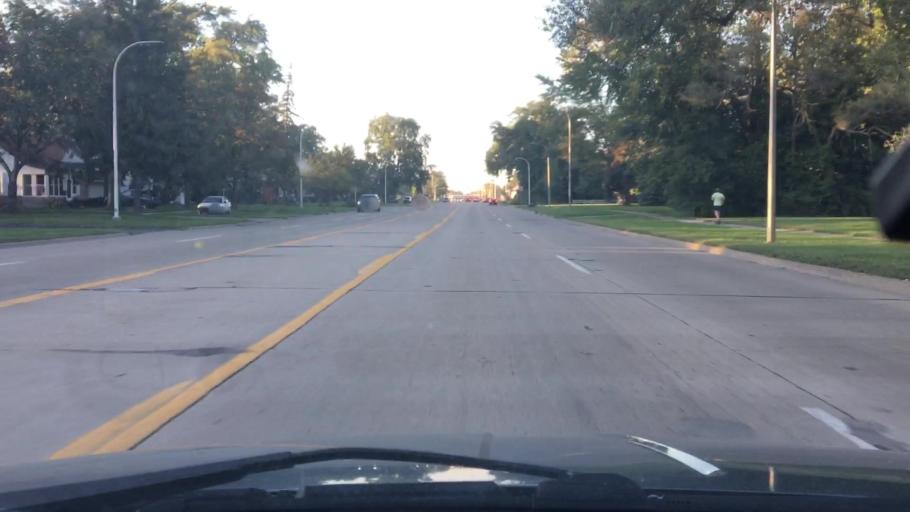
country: US
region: Michigan
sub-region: Wayne County
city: Livonia
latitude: 42.3651
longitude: -83.3522
